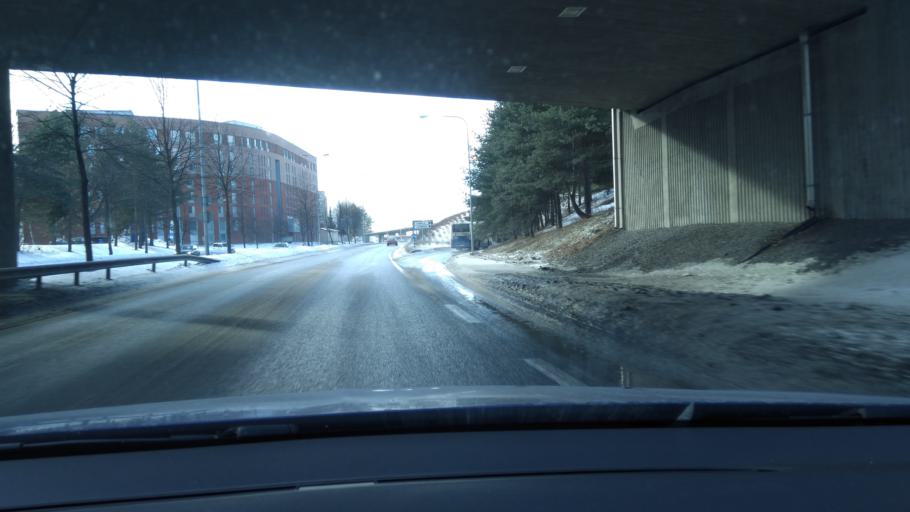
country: FI
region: Pirkanmaa
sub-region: Tampere
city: Tampere
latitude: 61.5065
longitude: 23.7865
